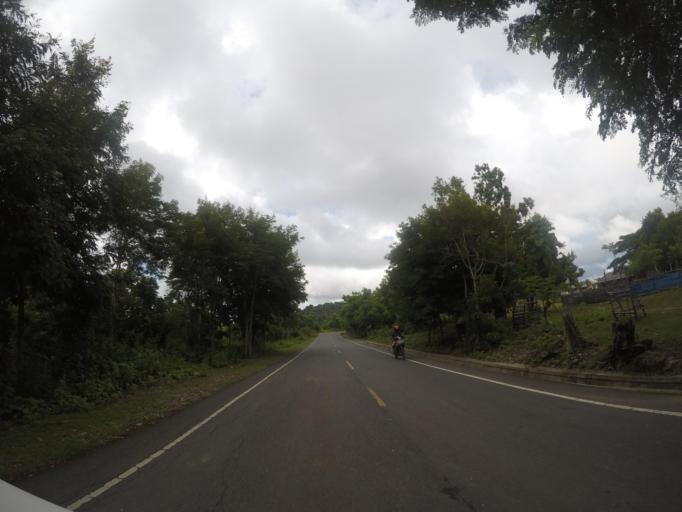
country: TL
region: Bobonaro
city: Maliana
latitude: -8.9664
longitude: 125.0385
